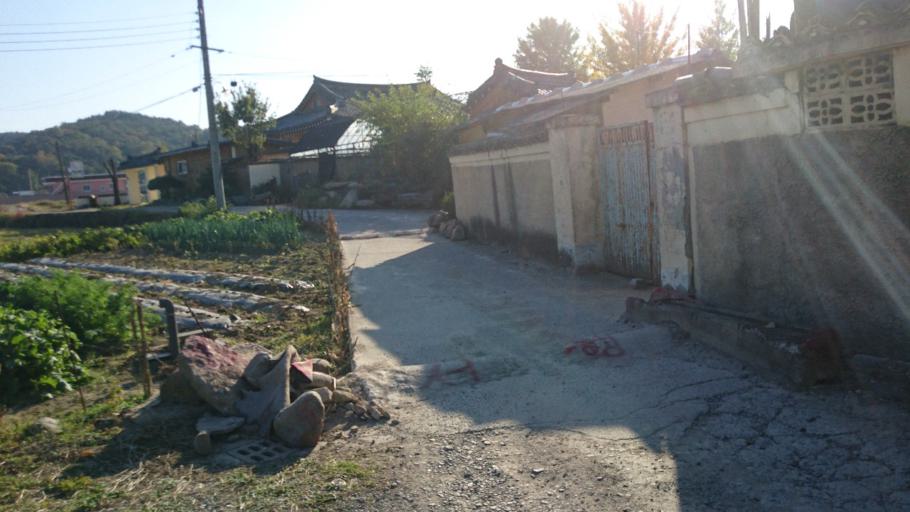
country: KR
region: Gyeongsangbuk-do
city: Kyonju
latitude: 35.8297
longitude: 129.2254
